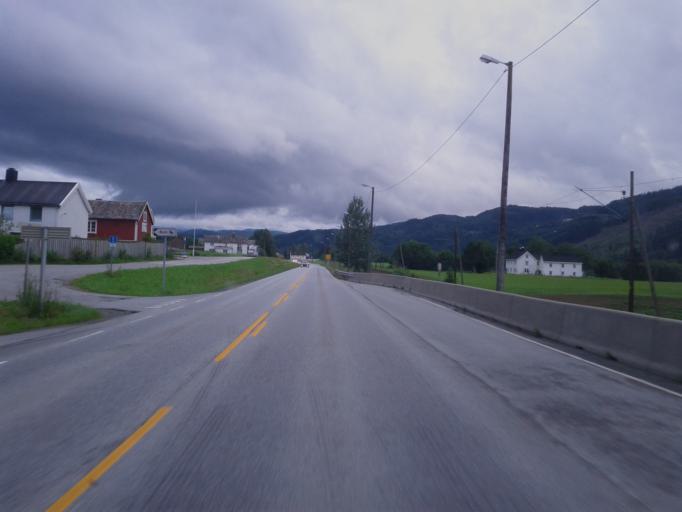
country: NO
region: Sor-Trondelag
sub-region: Melhus
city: Lundamo
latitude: 63.1488
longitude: 10.2709
